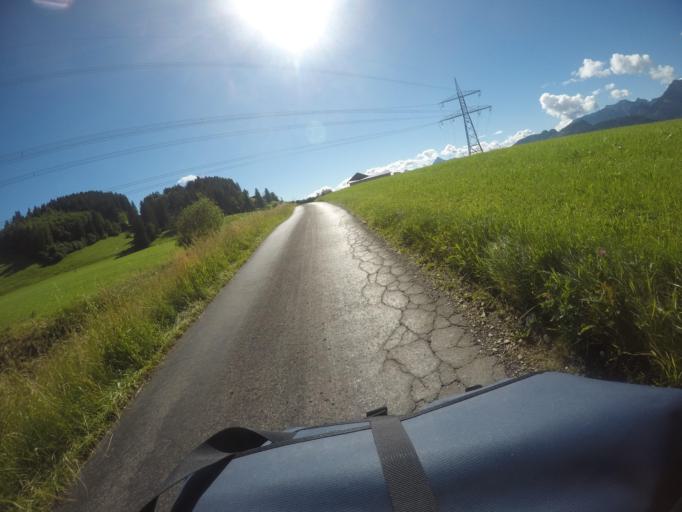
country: DE
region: Bavaria
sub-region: Swabia
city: Pfronten
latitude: 47.6070
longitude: 10.5504
